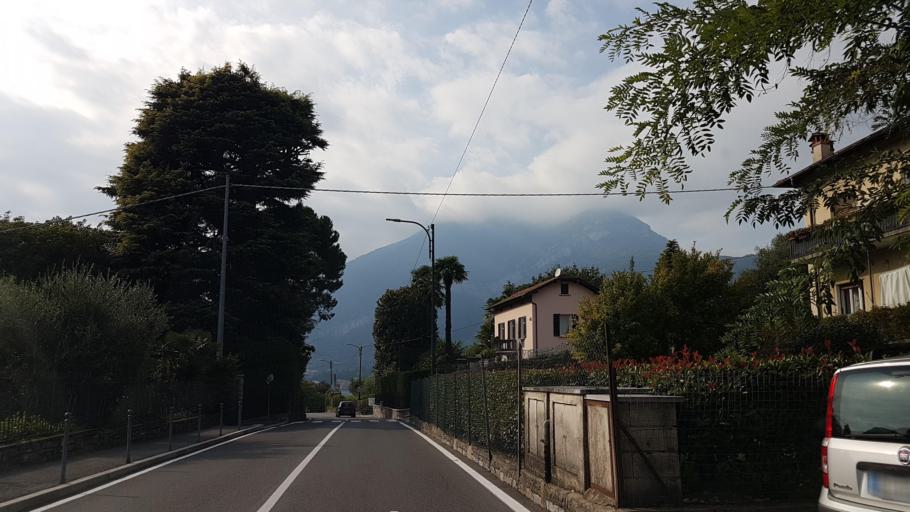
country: IT
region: Lombardy
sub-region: Provincia di Como
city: Bellagio
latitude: 45.9785
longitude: 9.2575
